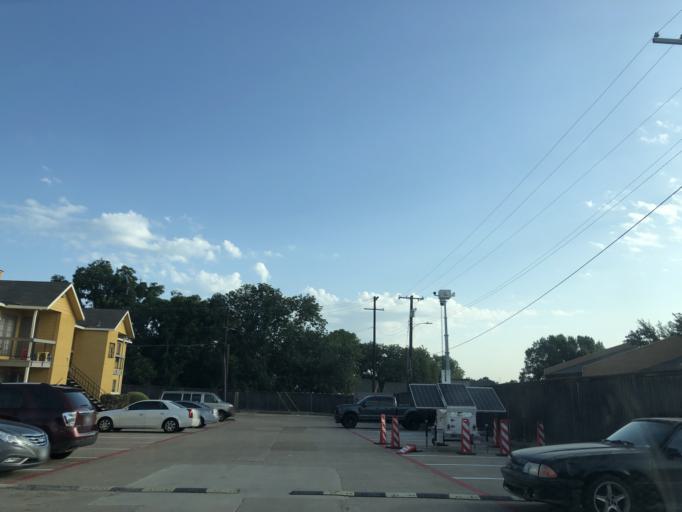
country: US
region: Texas
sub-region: Dallas County
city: Sunnyvale
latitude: 32.8438
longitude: -96.5898
